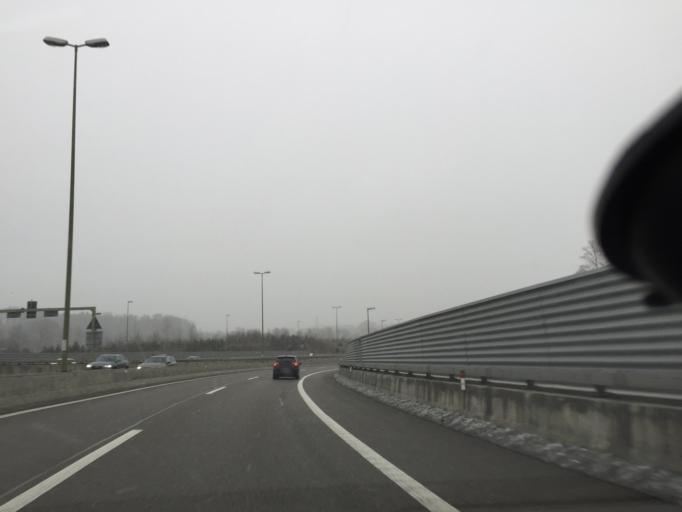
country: CH
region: Zurich
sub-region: Bezirk Zuerich
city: Zuerich (Kreis 2)
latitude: 47.3453
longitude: 8.5194
